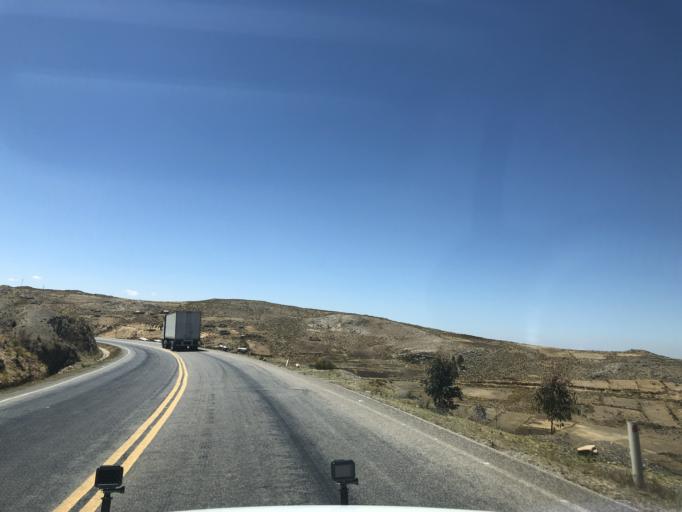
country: BO
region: Cochabamba
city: Irpa Irpa
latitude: -17.6678
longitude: -66.4820
